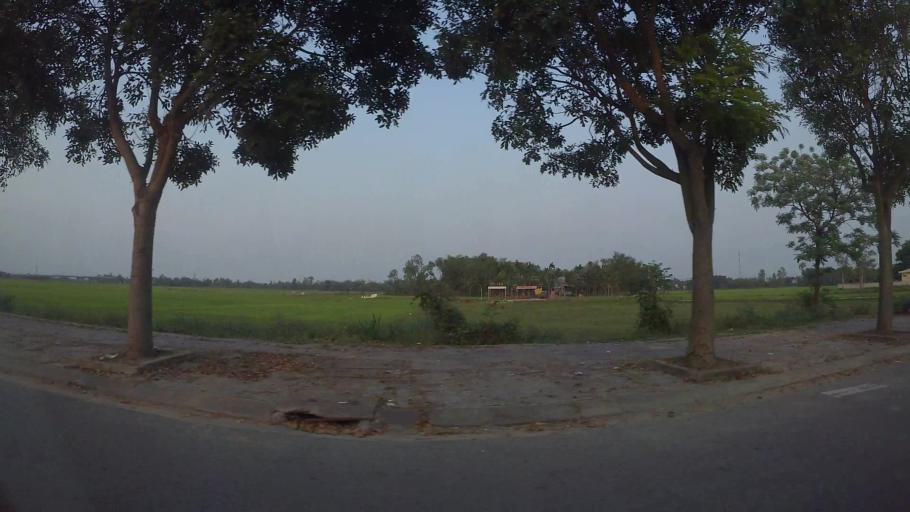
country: VN
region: Da Nang
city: Cam Le
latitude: 15.9599
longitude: 108.2143
